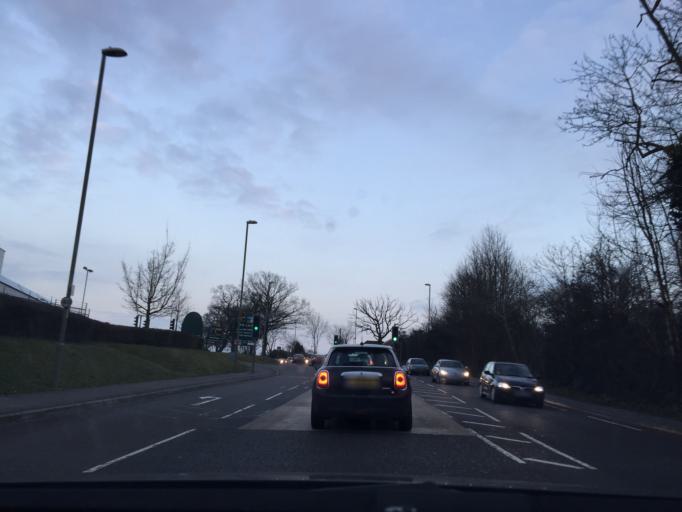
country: GB
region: England
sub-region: Hampshire
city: Fareham
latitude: 50.8369
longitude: -1.1796
